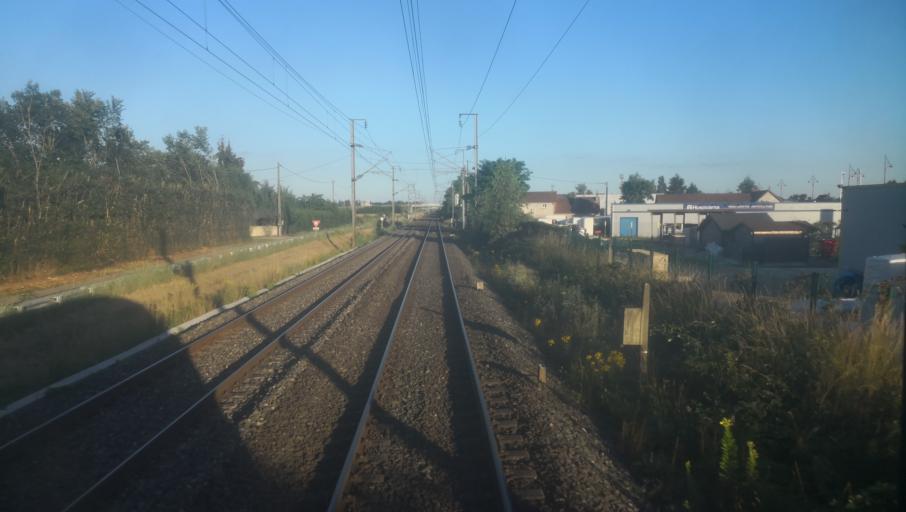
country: FR
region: Auvergne
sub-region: Departement de l'Allier
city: Avermes
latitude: 46.5941
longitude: 3.3114
